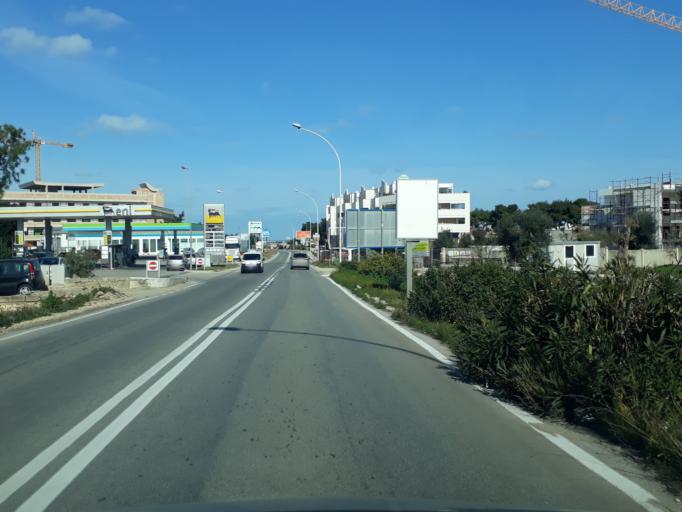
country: IT
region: Apulia
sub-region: Provincia di Bari
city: Monopoli
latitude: 40.9594
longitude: 17.2820
